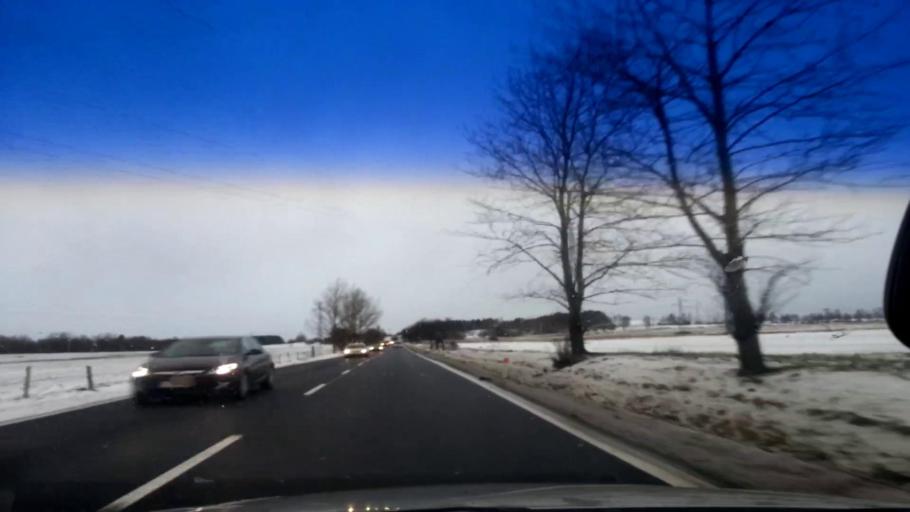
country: CZ
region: Karlovarsky
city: Hazlov
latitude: 50.1675
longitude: 12.2655
